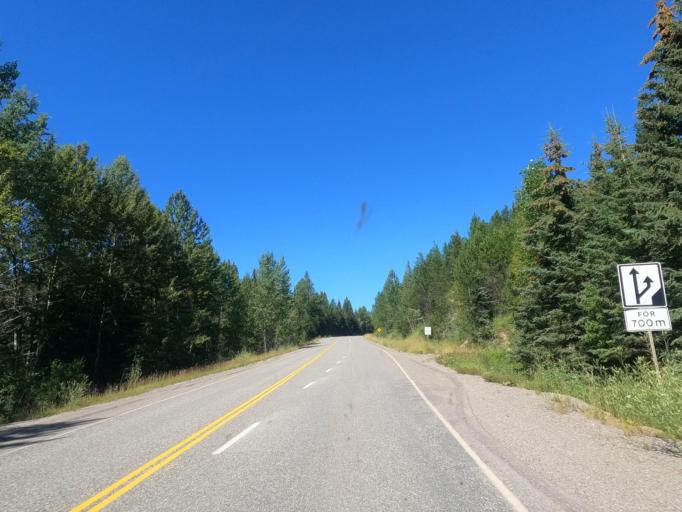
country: CA
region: British Columbia
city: Quesnel
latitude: 53.0514
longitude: -122.1881
